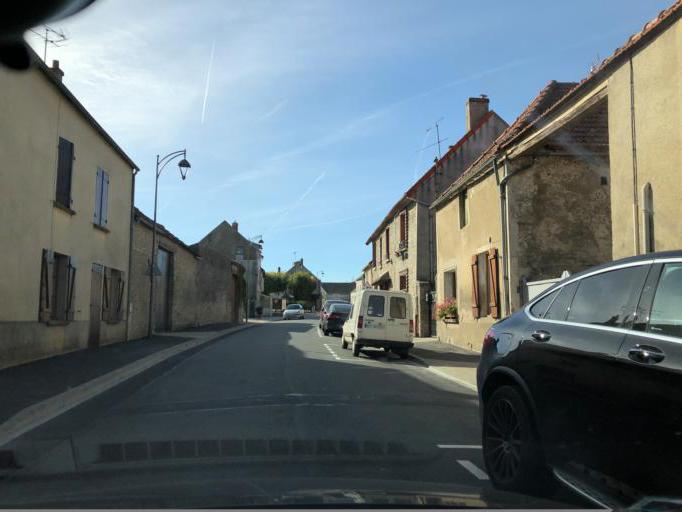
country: FR
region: Centre
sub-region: Departement du Loiret
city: Sermaises
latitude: 48.3570
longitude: 2.2719
